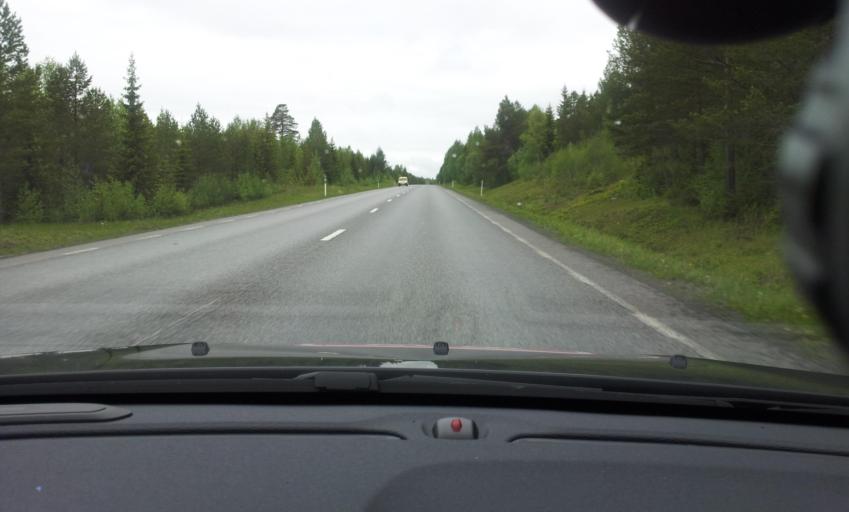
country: SE
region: Jaemtland
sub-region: Krokoms Kommun
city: Krokom
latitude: 63.3132
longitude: 14.1229
